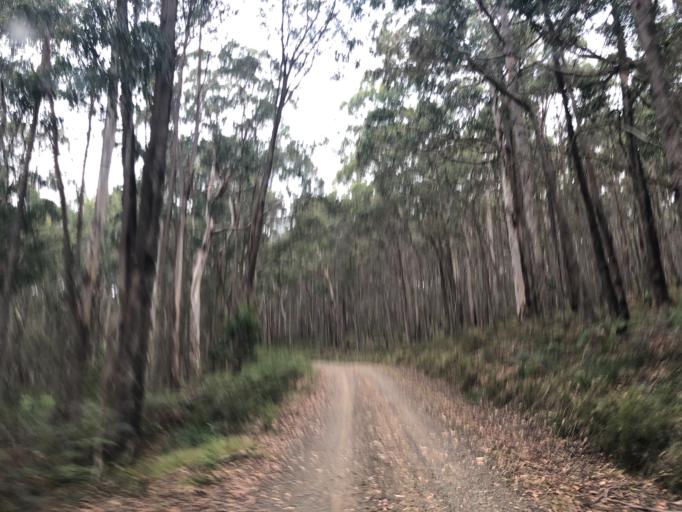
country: AU
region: Victoria
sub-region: Moorabool
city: Bacchus Marsh
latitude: -37.4360
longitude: 144.3406
